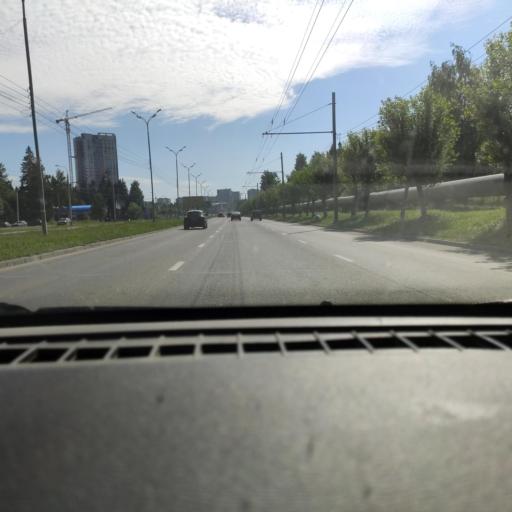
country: RU
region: Udmurtiya
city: Izhevsk
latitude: 56.8718
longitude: 53.2381
